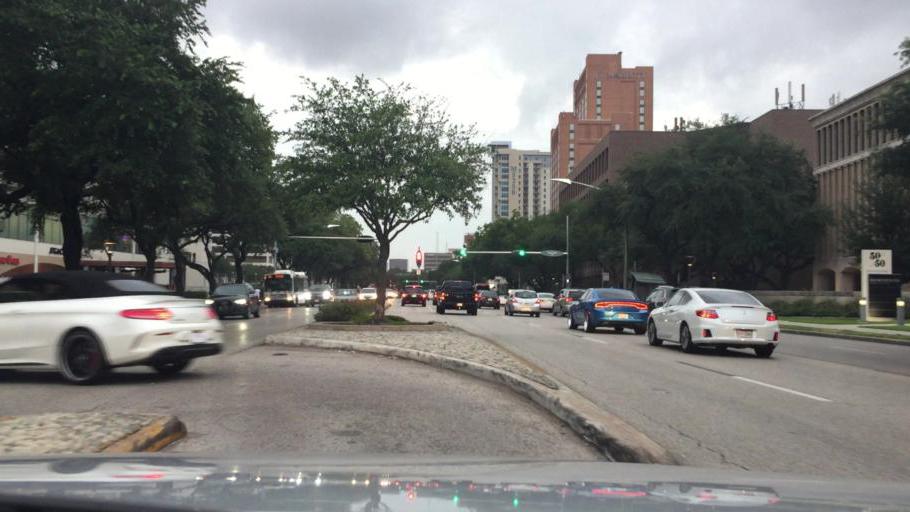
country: US
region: Texas
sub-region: Harris County
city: Bellaire
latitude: 29.7407
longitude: -95.4633
